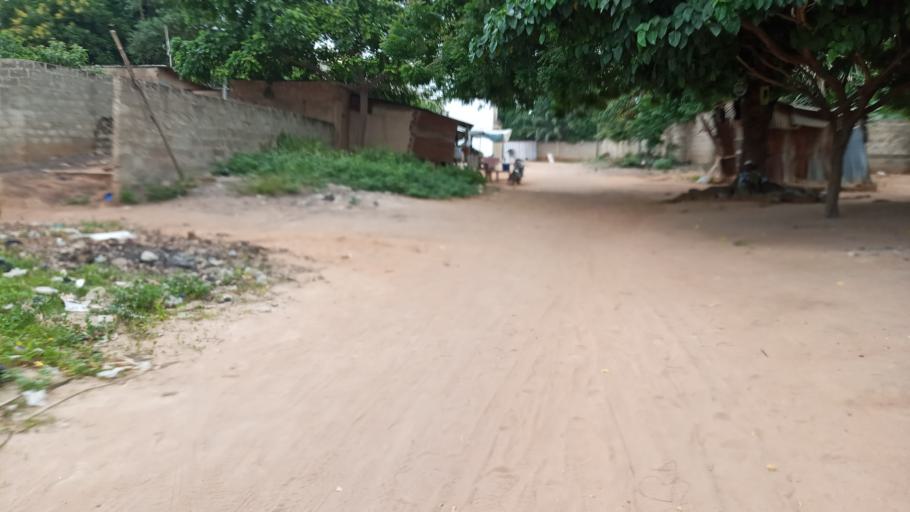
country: TG
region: Maritime
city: Lome
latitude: 6.1828
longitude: 1.1714
